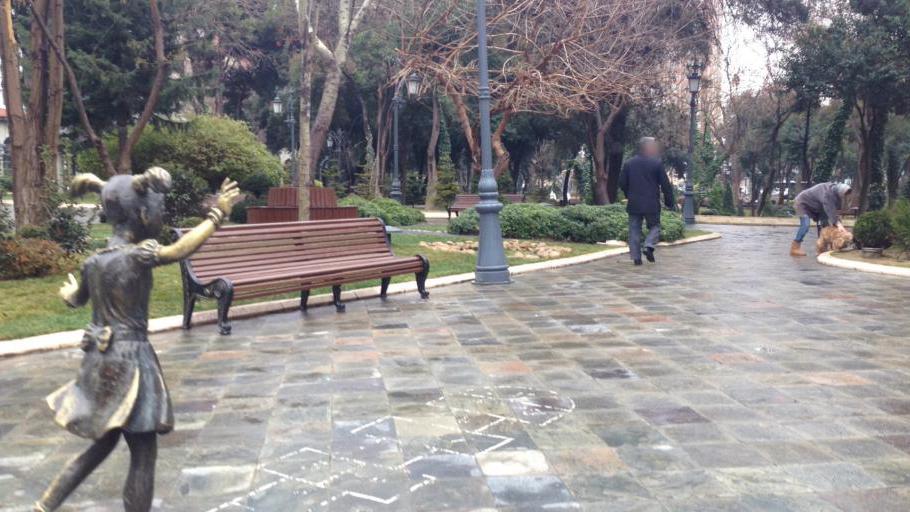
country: AZ
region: Baki
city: Badamdar
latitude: 40.3846
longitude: 49.8358
